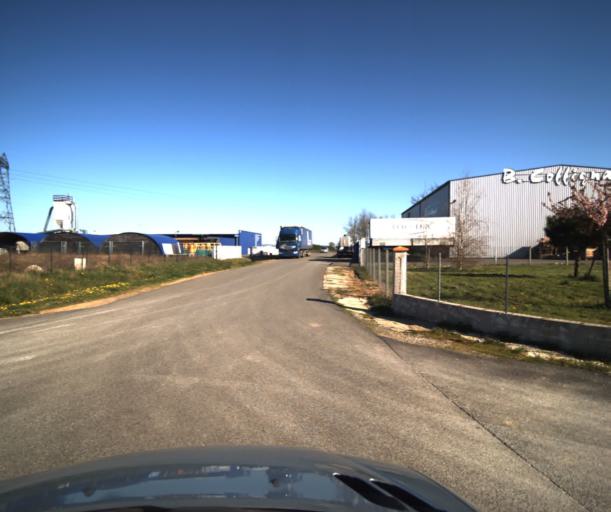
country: FR
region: Midi-Pyrenees
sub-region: Departement du Tarn-et-Garonne
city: Bressols
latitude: 43.9484
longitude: 1.3266
